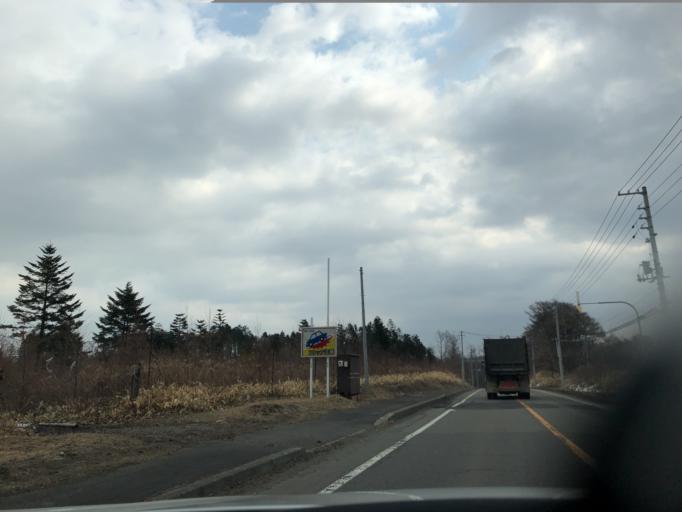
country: JP
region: Hokkaido
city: Chitose
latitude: 42.7587
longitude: 141.7908
